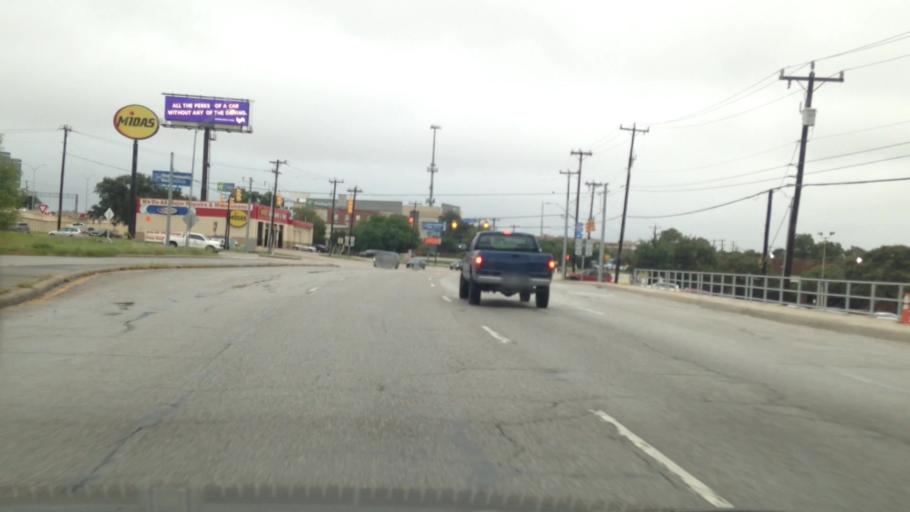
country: US
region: Texas
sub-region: Bexar County
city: Shavano Park
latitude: 29.5470
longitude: -98.5838
